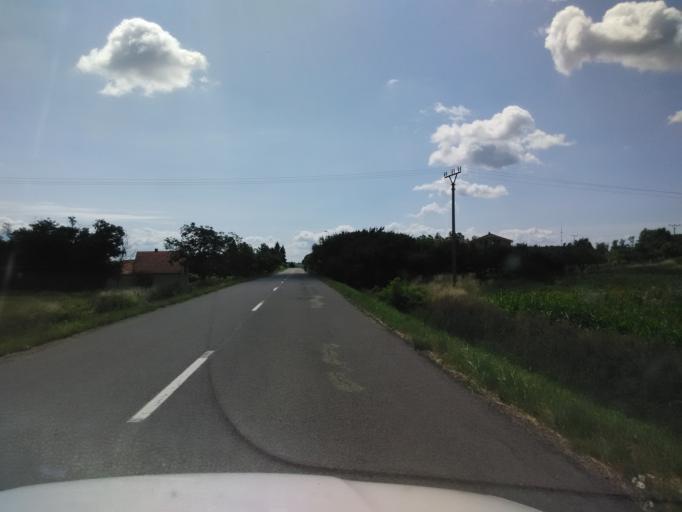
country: SK
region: Nitriansky
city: Levice
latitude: 48.2848
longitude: 18.6874
